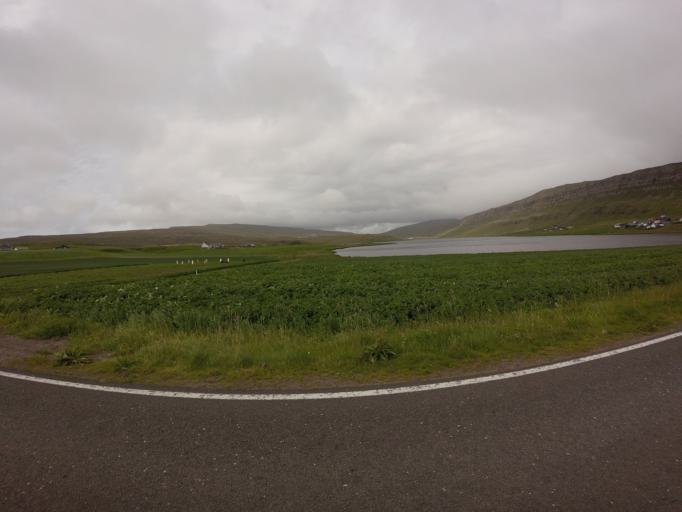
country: FO
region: Sandoy
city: Sandur
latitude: 61.8386
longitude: -6.8146
